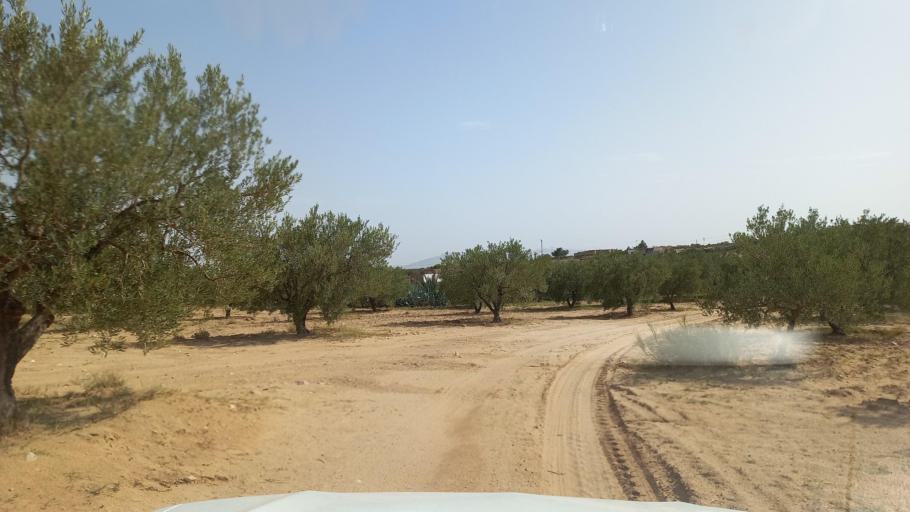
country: TN
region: Al Qasrayn
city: Kasserine
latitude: 35.3000
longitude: 8.9561
